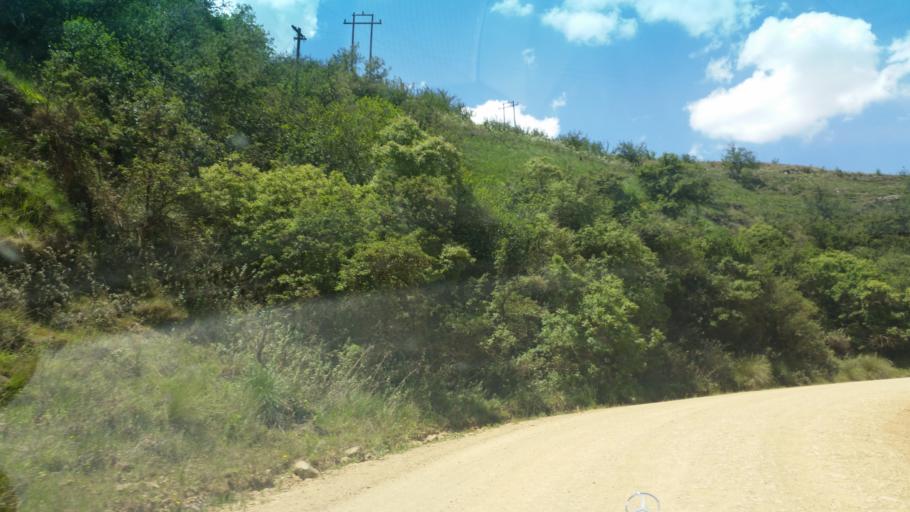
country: ZA
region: KwaZulu-Natal
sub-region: uMgungundlovu District Municipality
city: Impendle
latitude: -29.4551
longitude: 29.7432
